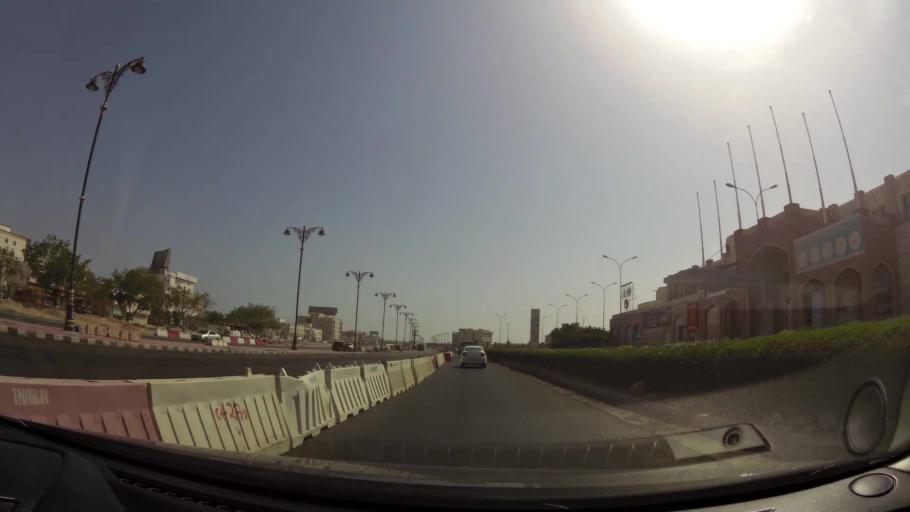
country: OM
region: Zufar
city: Salalah
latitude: 17.0218
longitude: 54.0665
